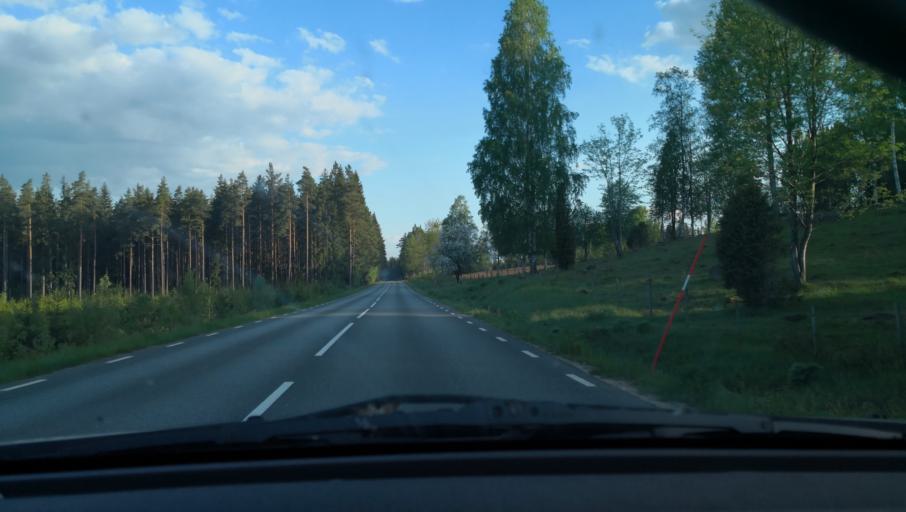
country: SE
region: Joenkoeping
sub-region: Vetlanda Kommun
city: Landsbro
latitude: 57.3796
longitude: 14.8581
